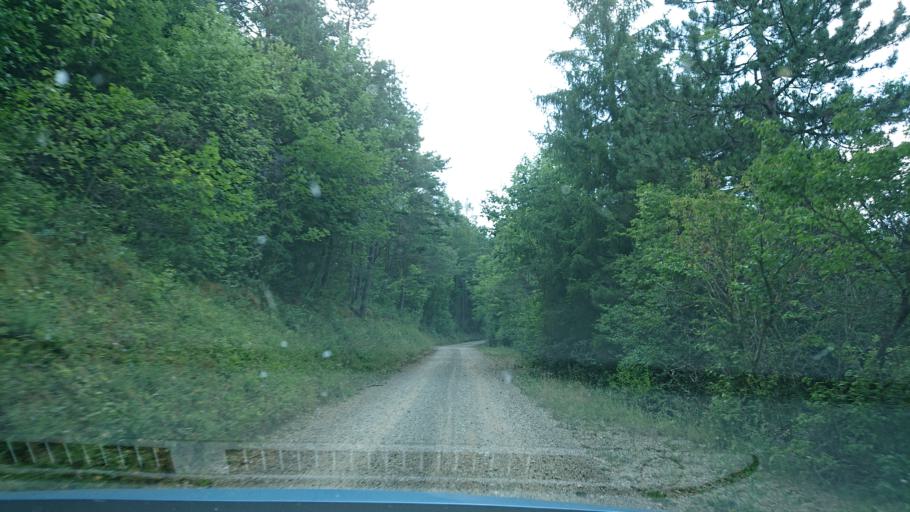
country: FR
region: Rhone-Alpes
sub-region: Departement de l'Isere
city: Mens
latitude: 44.7980
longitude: 5.8951
